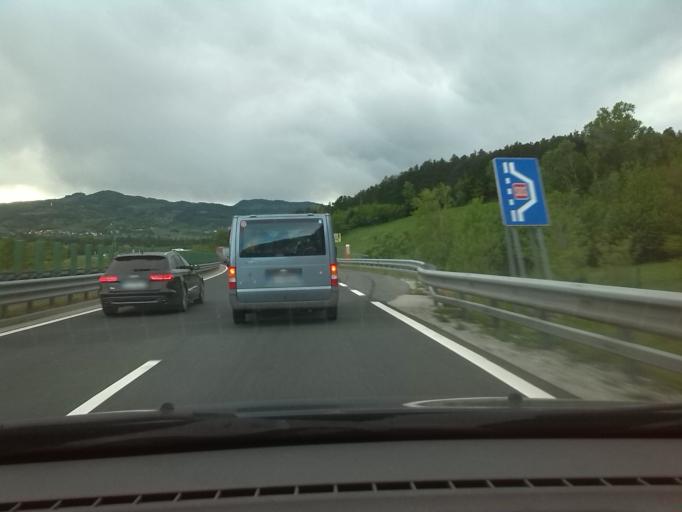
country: SI
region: Vipava
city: Vipava
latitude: 45.8115
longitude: 13.9746
